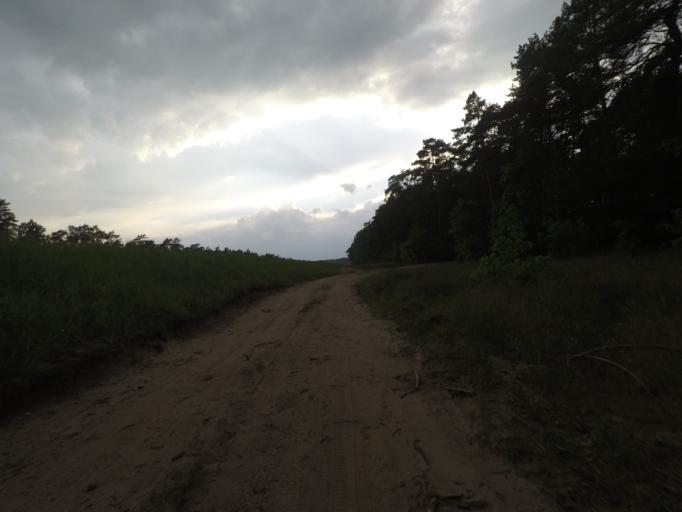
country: DE
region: Brandenburg
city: Melchow
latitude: 52.8599
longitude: 13.7158
